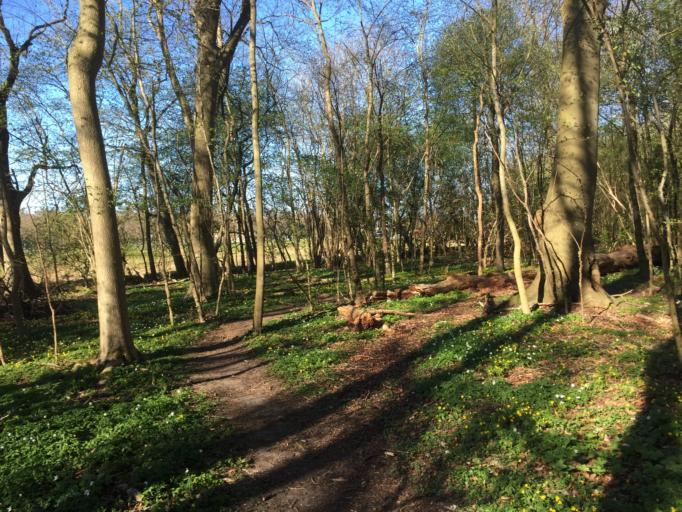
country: DK
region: South Denmark
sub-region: Odense Kommune
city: Neder Holluf
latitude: 55.3726
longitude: 10.4208
